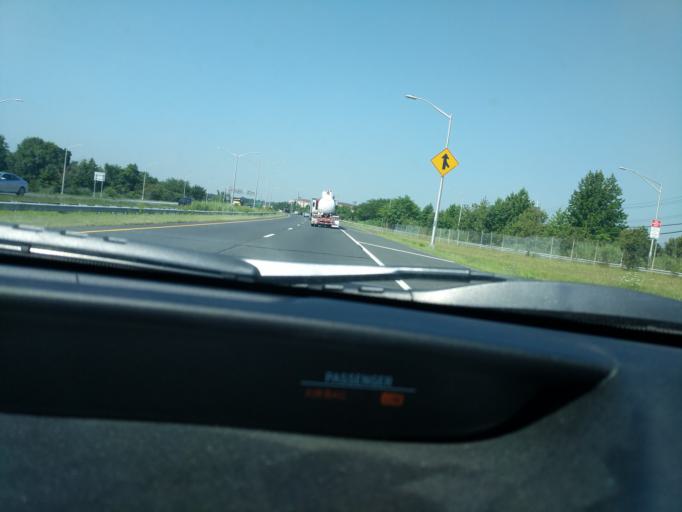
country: US
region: New Jersey
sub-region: Middlesex County
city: Carteret
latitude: 40.5562
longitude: -74.2096
